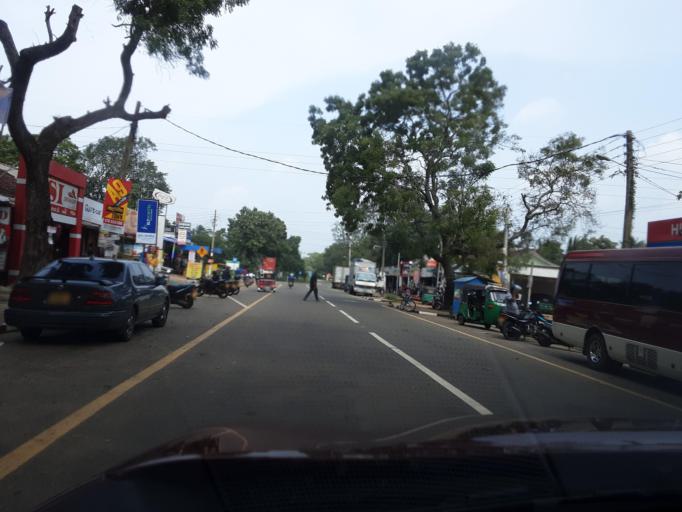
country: LK
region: North Central
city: Anuradhapura
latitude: 8.3588
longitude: 80.5116
